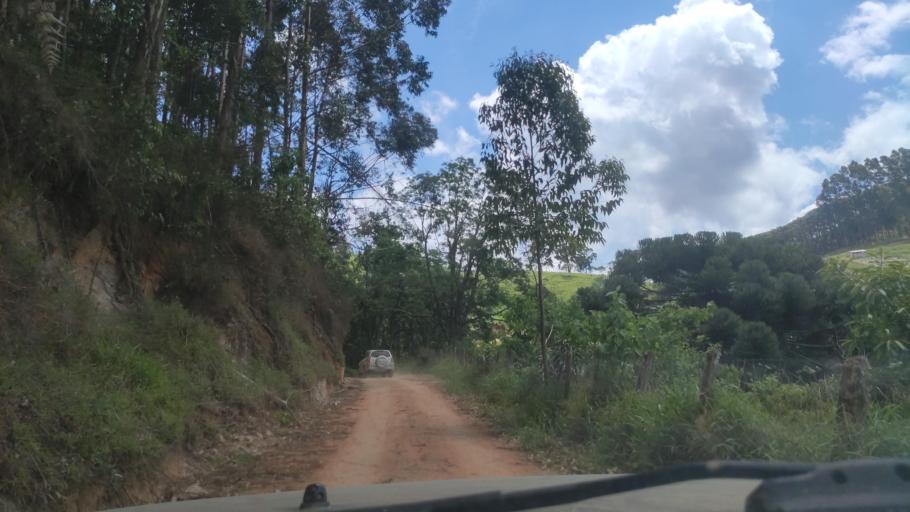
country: BR
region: Minas Gerais
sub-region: Cambui
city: Cambui
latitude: -22.6787
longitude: -45.9690
